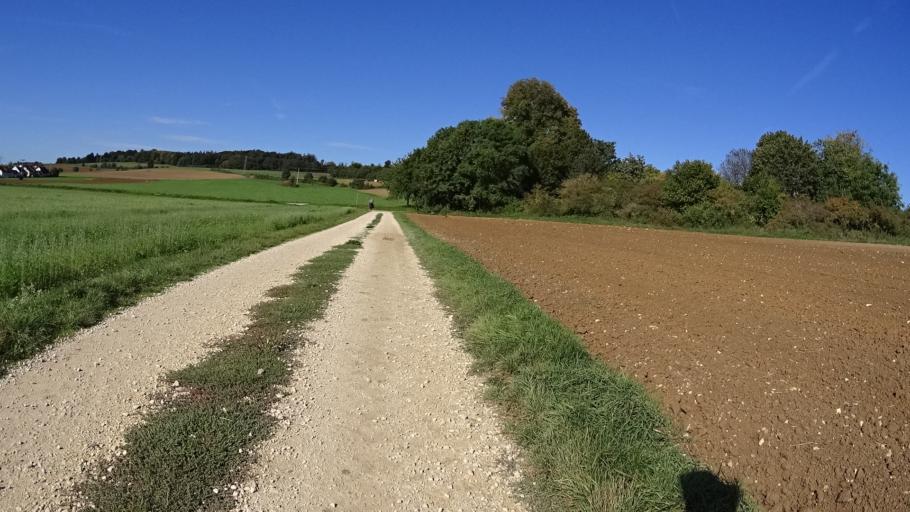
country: DE
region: Bavaria
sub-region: Upper Bavaria
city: Adelschlag
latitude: 48.8666
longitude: 11.2422
